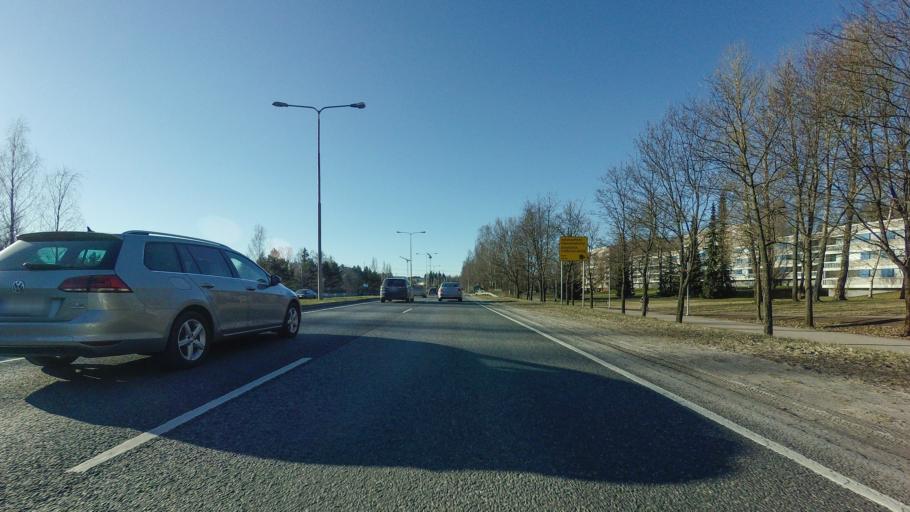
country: FI
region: Uusimaa
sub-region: Helsinki
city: Vantaa
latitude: 60.2168
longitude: 25.0843
